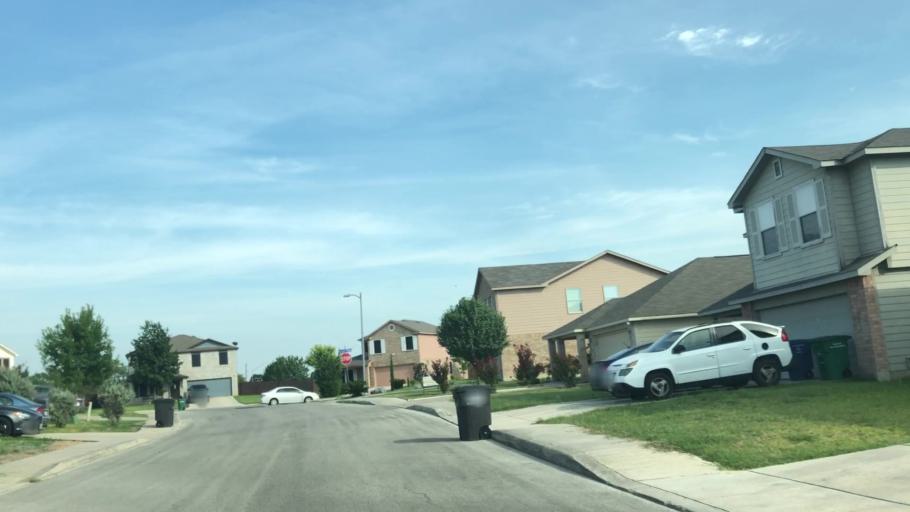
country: US
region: Texas
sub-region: Bexar County
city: Helotes
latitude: 29.5550
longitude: -98.6500
